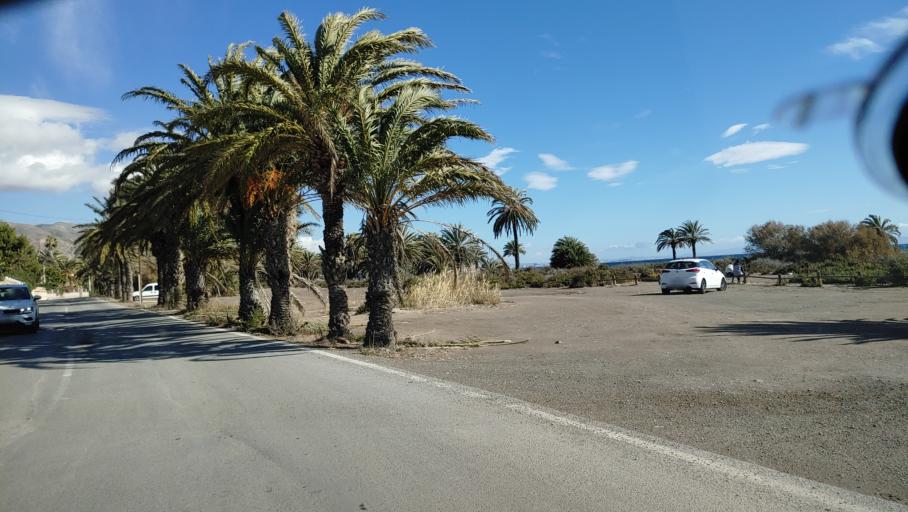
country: ES
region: Andalusia
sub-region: Provincia de Almeria
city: Aguadulce
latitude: 36.7922
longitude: -2.5879
